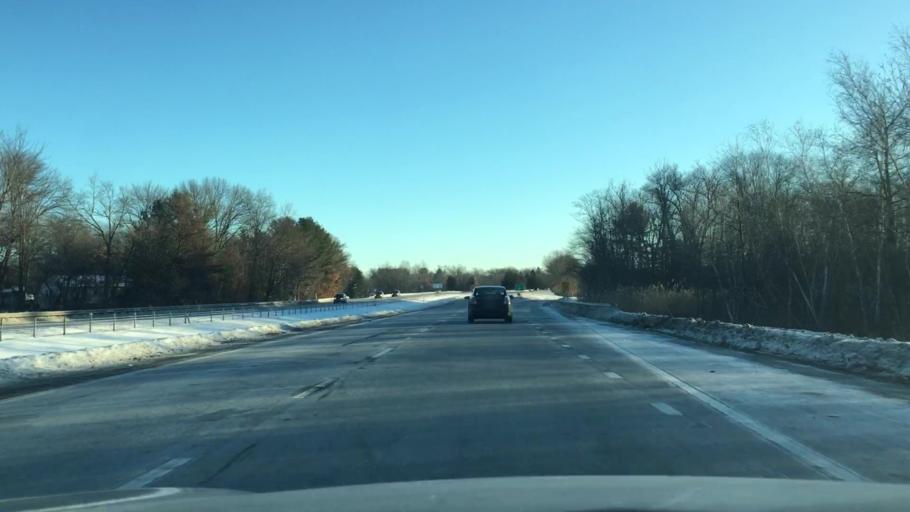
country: US
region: Massachusetts
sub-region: Hampden County
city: Agawam
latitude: 42.0723
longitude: -72.6362
